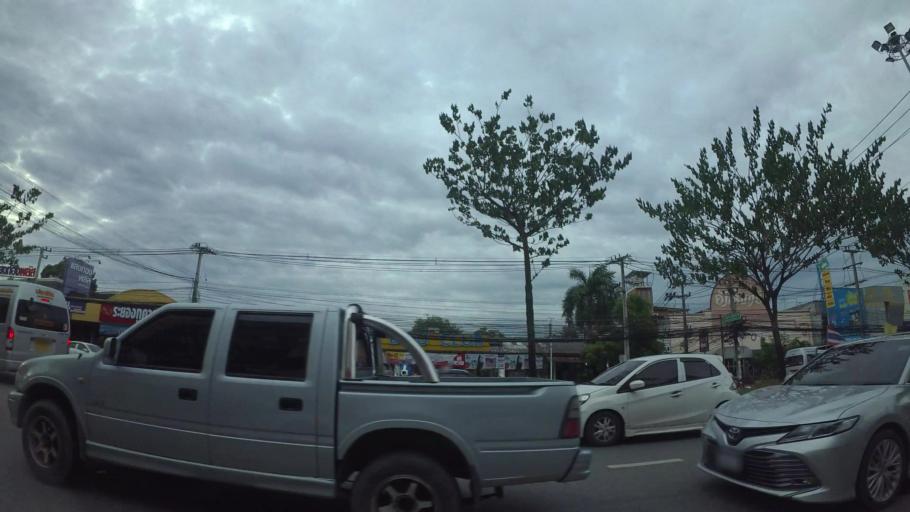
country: TH
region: Rayong
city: Rayong
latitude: 12.6873
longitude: 101.2638
